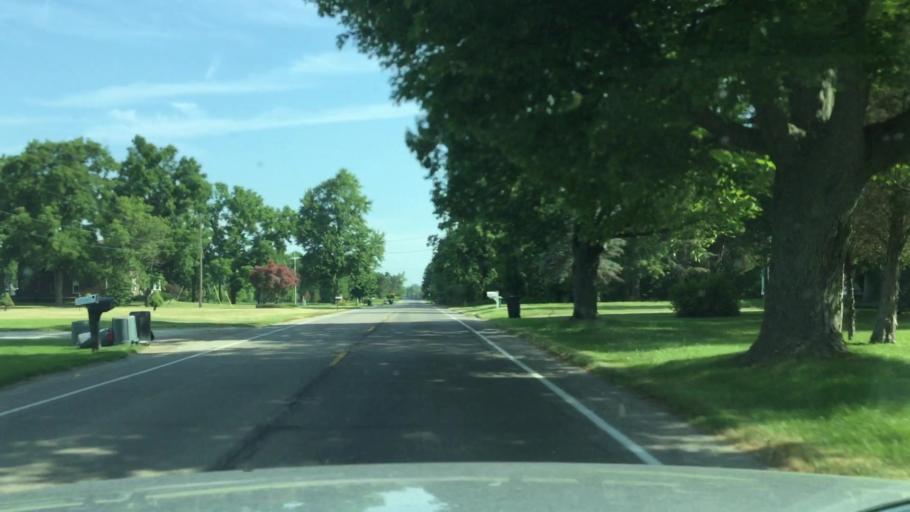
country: US
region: Michigan
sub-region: Genesee County
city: Flushing
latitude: 43.1109
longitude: -83.8728
